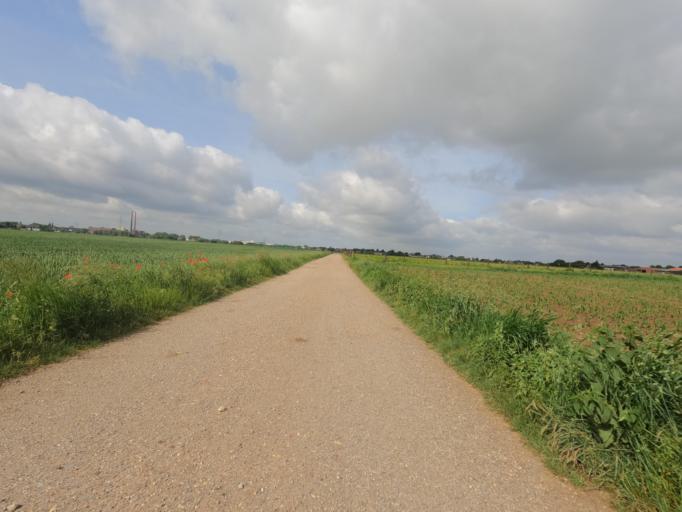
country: DE
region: North Rhine-Westphalia
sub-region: Regierungsbezirk Koln
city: Wassenberg
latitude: 51.0705
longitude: 6.1493
